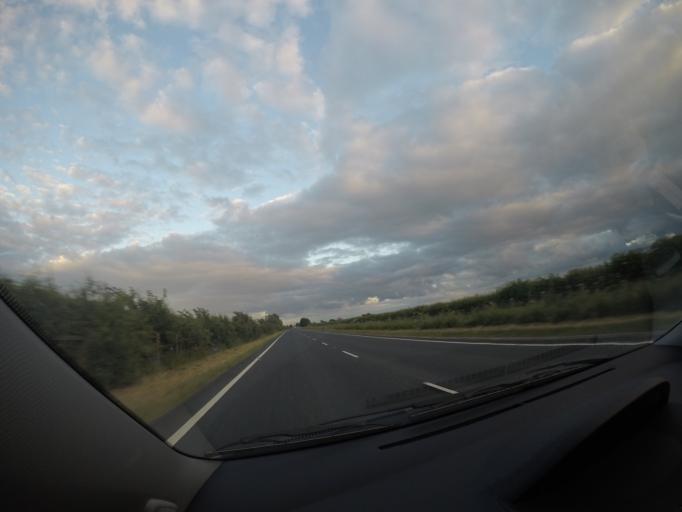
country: GB
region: England
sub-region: North Yorkshire
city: Bedale
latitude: 54.2529
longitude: -1.5101
